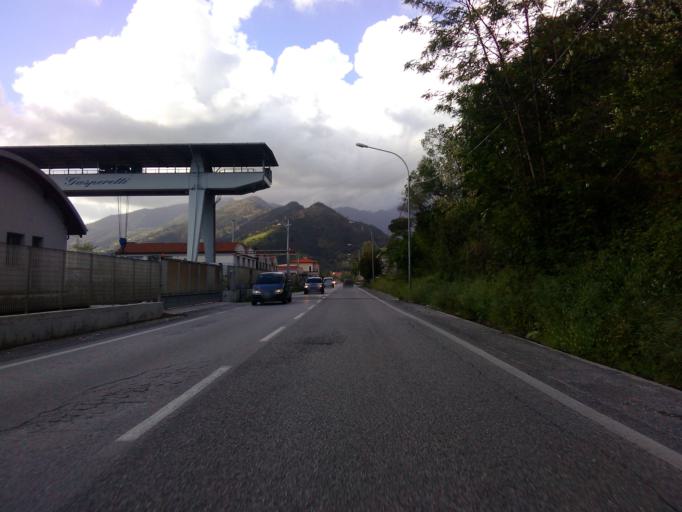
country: IT
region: Tuscany
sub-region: Provincia di Lucca
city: Ripa-Pozzi-Querceta-Ponterosso
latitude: 43.9735
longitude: 10.2203
